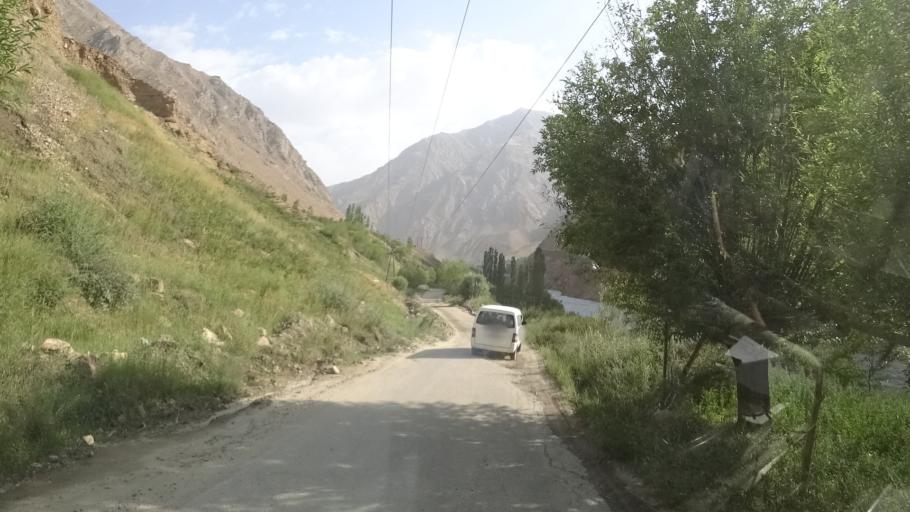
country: TJ
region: Gorno-Badakhshan
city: Khorugh
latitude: 37.3488
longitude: 71.4919
